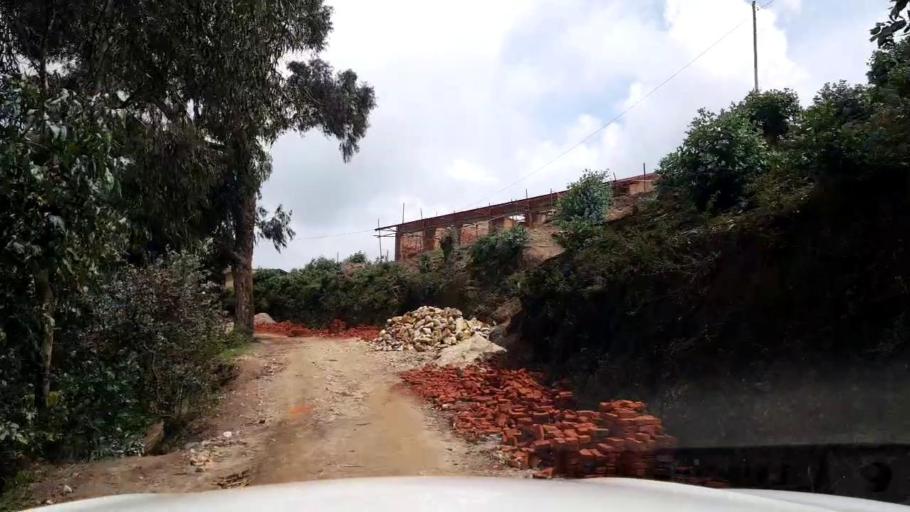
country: RW
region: Western Province
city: Kibuye
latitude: -1.9377
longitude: 29.4584
